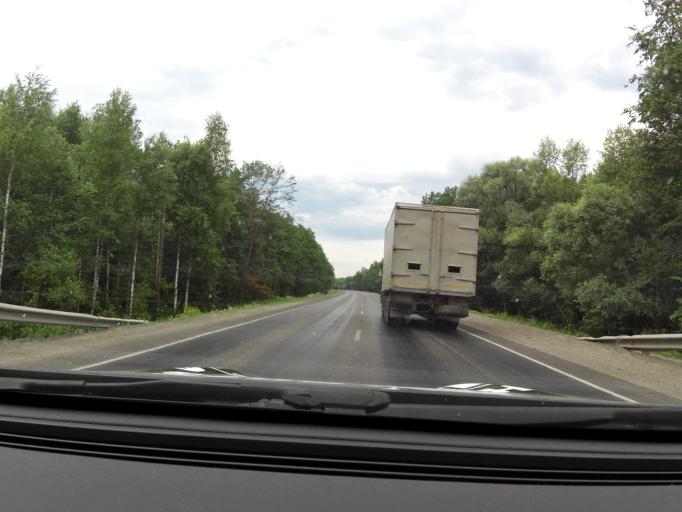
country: RU
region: Bashkortostan
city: Urman
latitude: 54.8314
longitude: 56.9444
